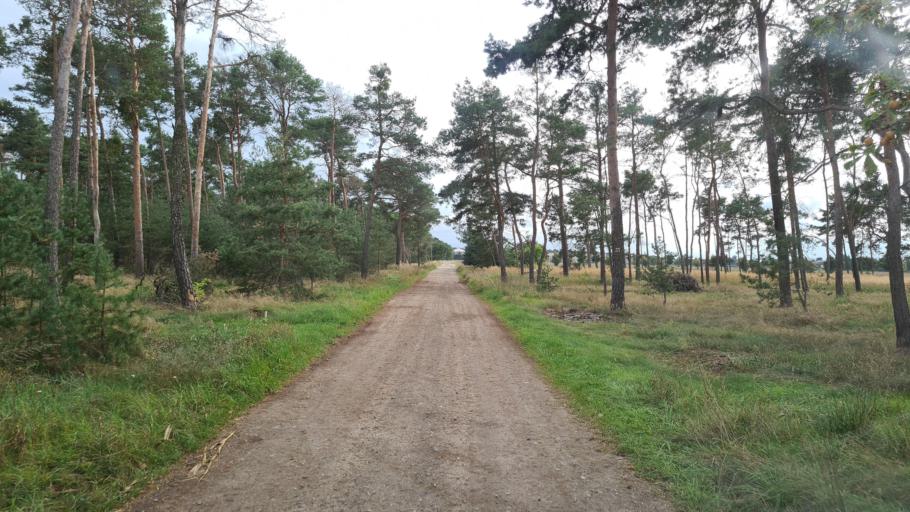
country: DE
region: Brandenburg
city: Bad Liebenwerda
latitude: 51.4718
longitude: 13.3965
